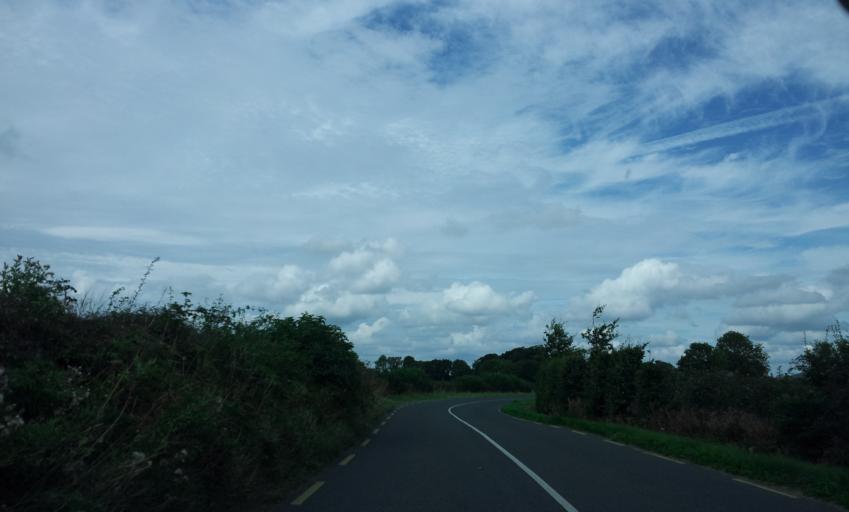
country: IE
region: Leinster
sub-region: Laois
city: Stradbally
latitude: 52.9728
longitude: -7.2129
